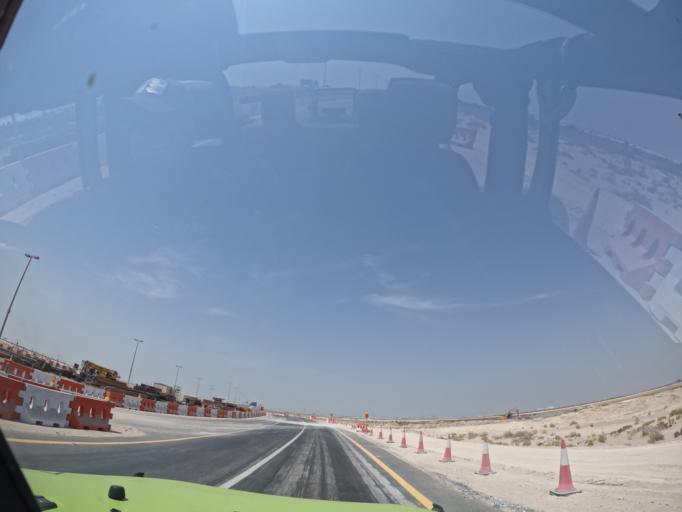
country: AE
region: Abu Dhabi
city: Abu Dhabi
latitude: 24.2393
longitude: 54.4825
